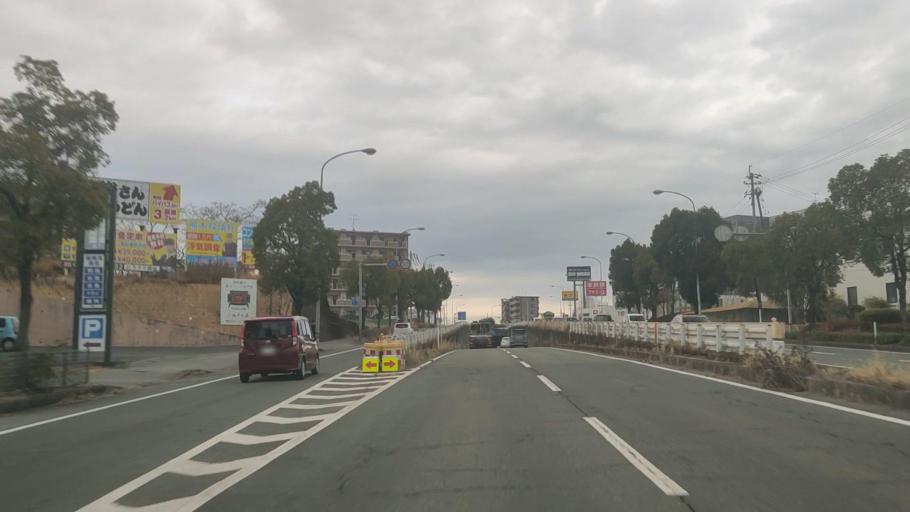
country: JP
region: Kumamoto
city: Ozu
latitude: 32.8511
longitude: 130.7829
